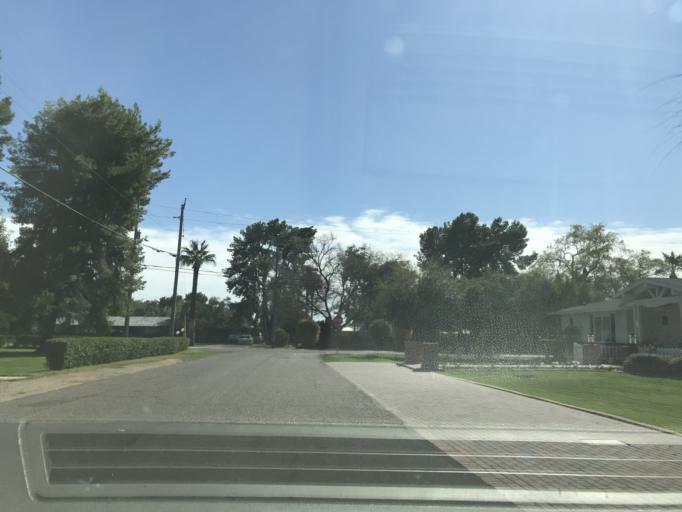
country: US
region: Arizona
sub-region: Maricopa County
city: Phoenix
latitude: 33.5171
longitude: -112.0683
